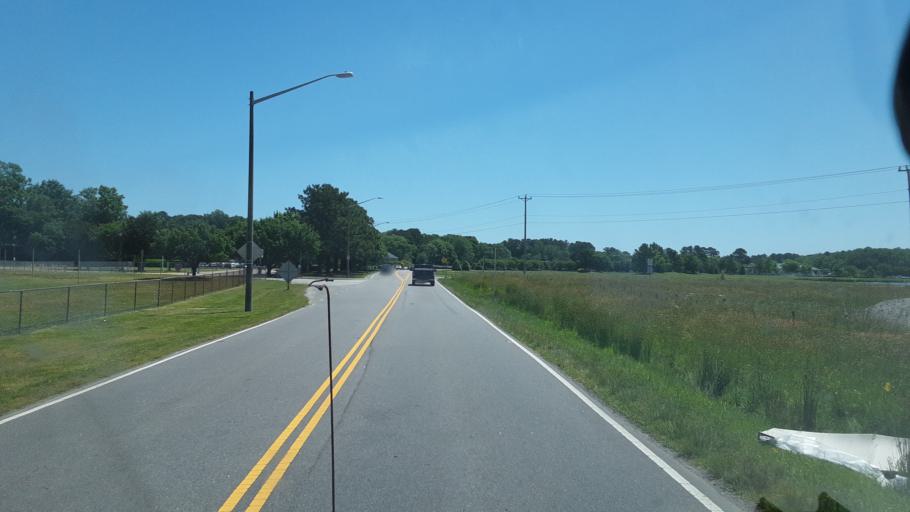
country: US
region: Virginia
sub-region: City of Virginia Beach
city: Virginia Beach
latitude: 36.7470
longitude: -76.0021
